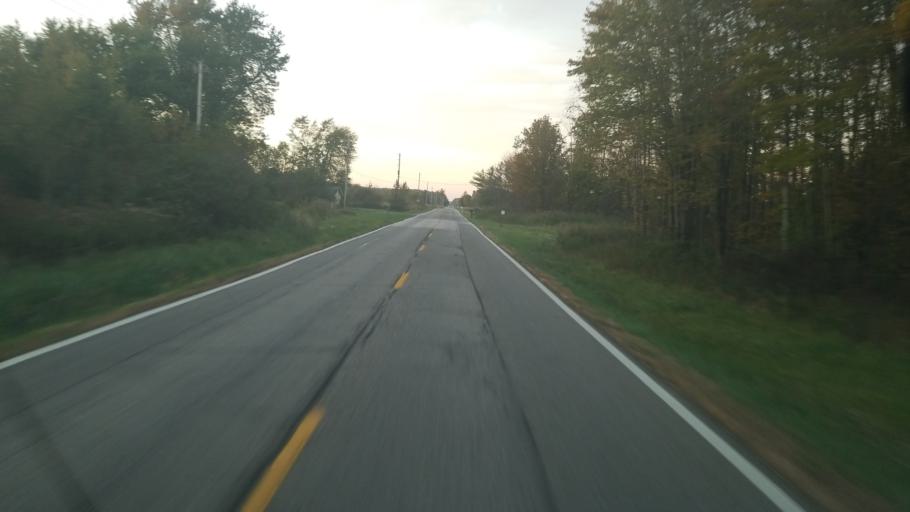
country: US
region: Ohio
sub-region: Ashtabula County
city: Andover
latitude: 41.6359
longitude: -80.6668
